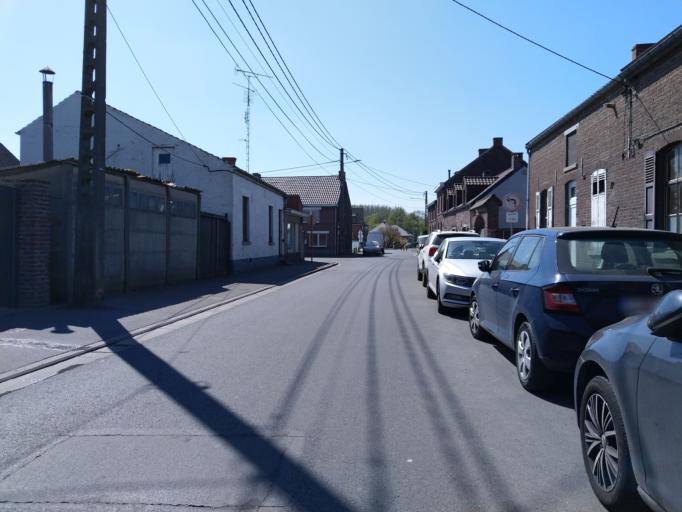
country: BE
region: Wallonia
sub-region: Province du Hainaut
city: Mons
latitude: 50.4763
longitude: 4.0084
